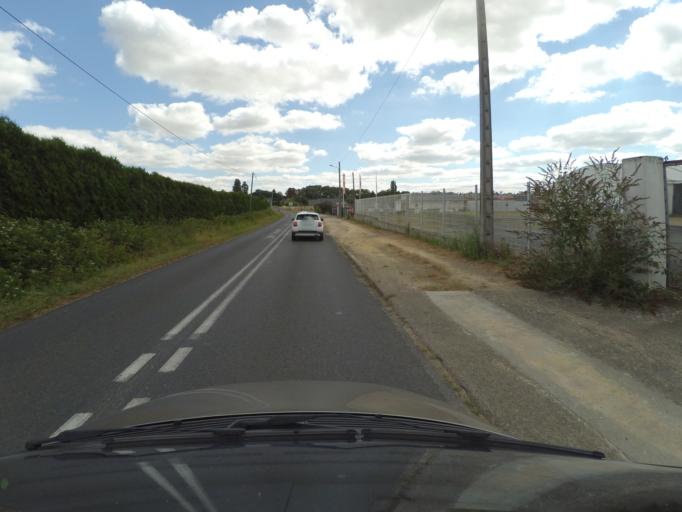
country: FR
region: Pays de la Loire
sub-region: Departement de Maine-et-Loire
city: Doue-la-Fontaine
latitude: 47.2020
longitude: -0.2759
